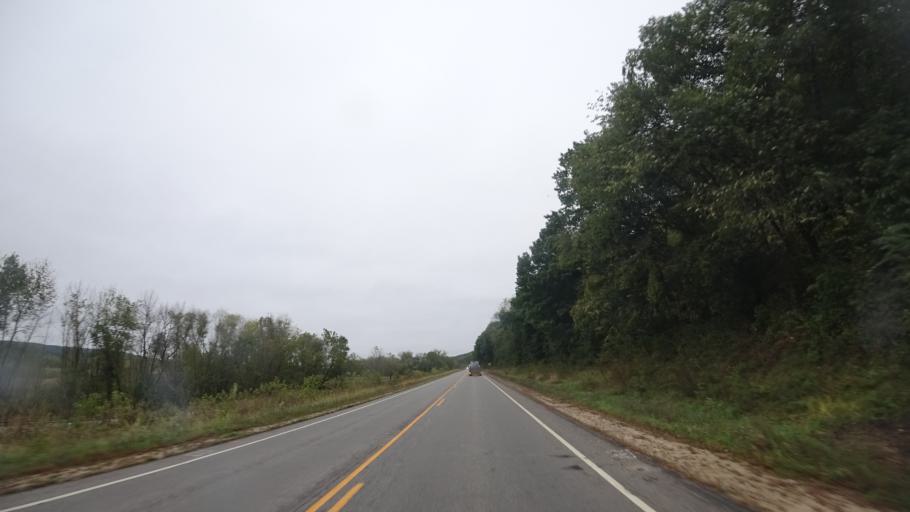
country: US
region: Wisconsin
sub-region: Crawford County
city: Prairie du Chien
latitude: 43.0759
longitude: -90.9341
